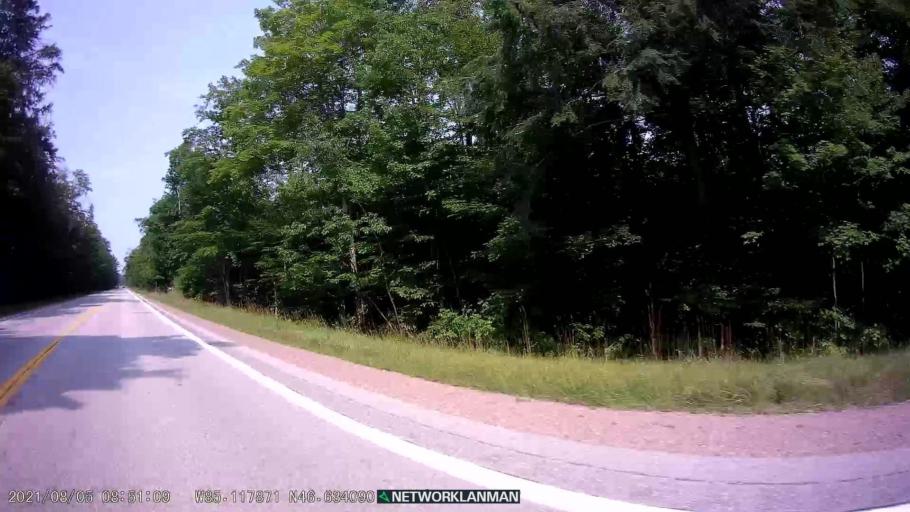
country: US
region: Michigan
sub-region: Luce County
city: Newberry
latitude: 46.6341
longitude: -85.1180
